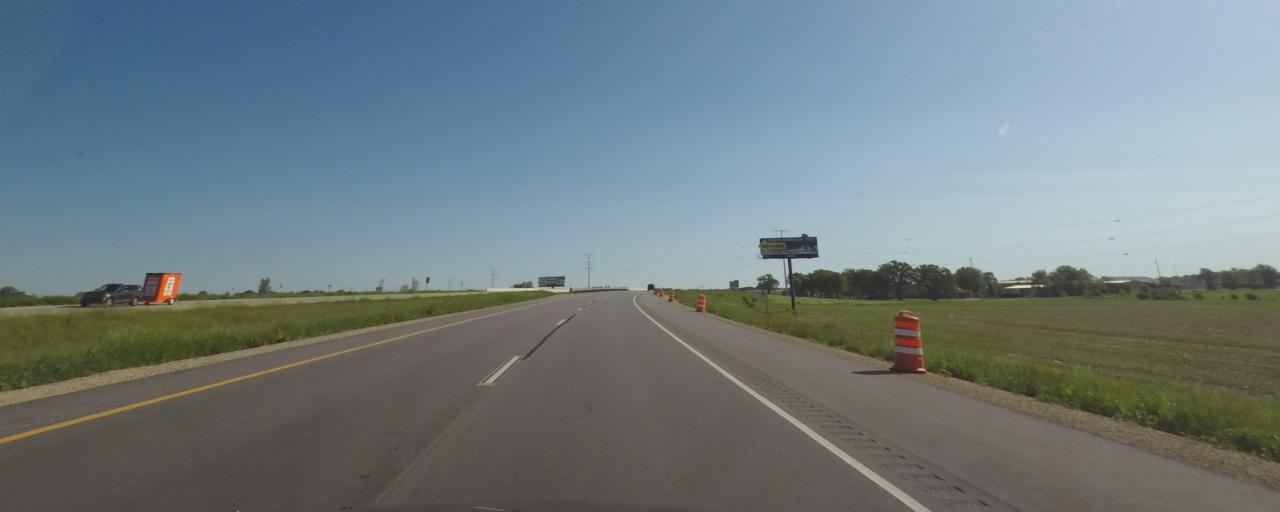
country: US
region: Wisconsin
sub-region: Columbia County
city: Columbus
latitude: 43.3399
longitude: -89.0427
